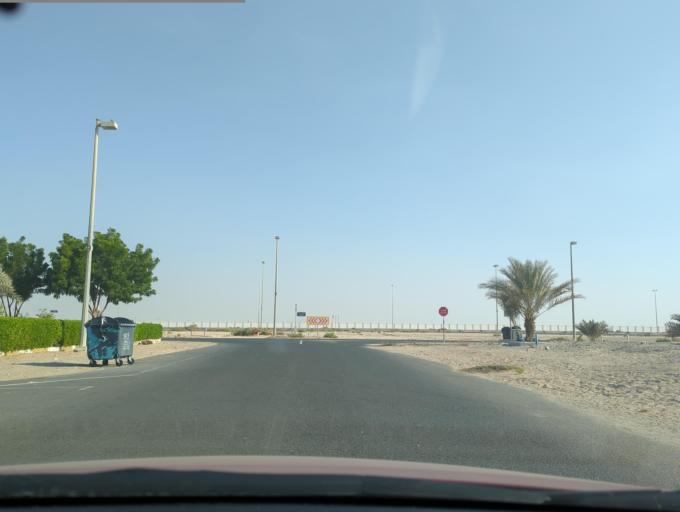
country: AE
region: Abu Dhabi
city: Abu Dhabi
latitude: 24.3961
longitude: 54.7444
